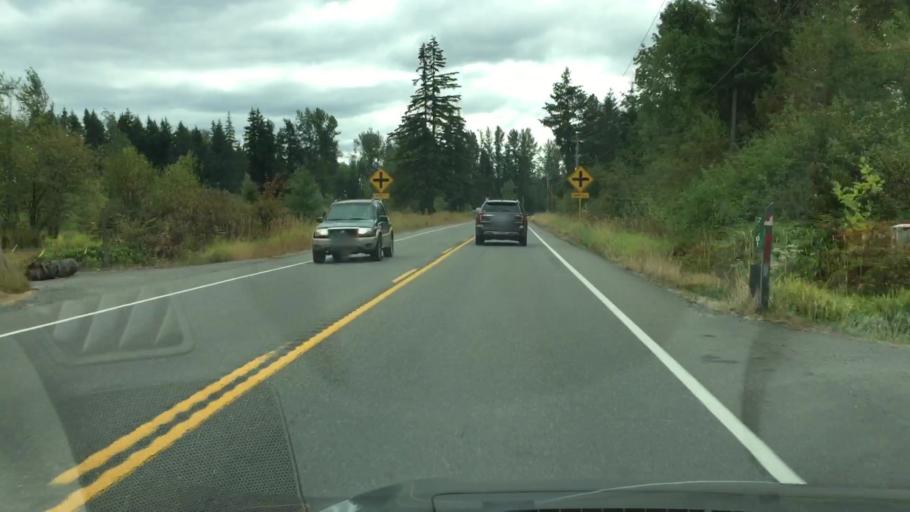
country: US
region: Washington
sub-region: Pierce County
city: Graham
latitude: 46.9971
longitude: -122.2957
